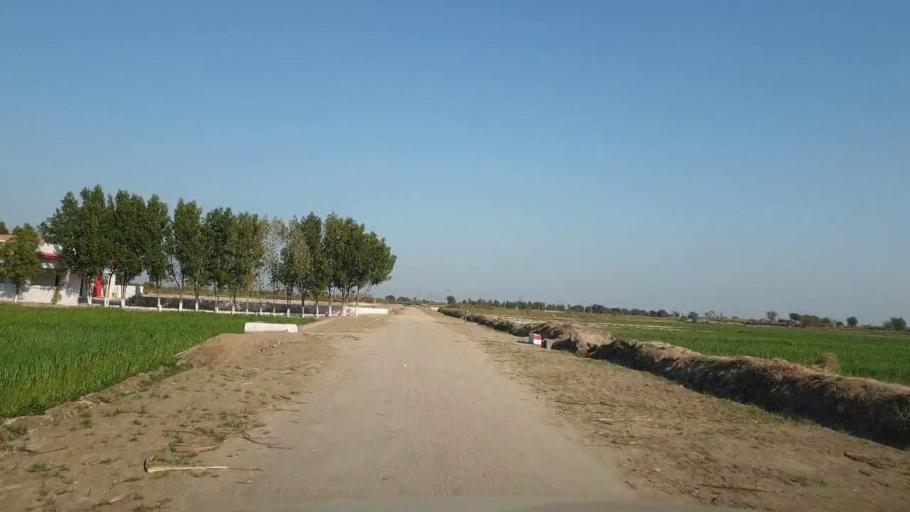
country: PK
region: Sindh
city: Tando Allahyar
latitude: 25.5066
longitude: 68.6615
